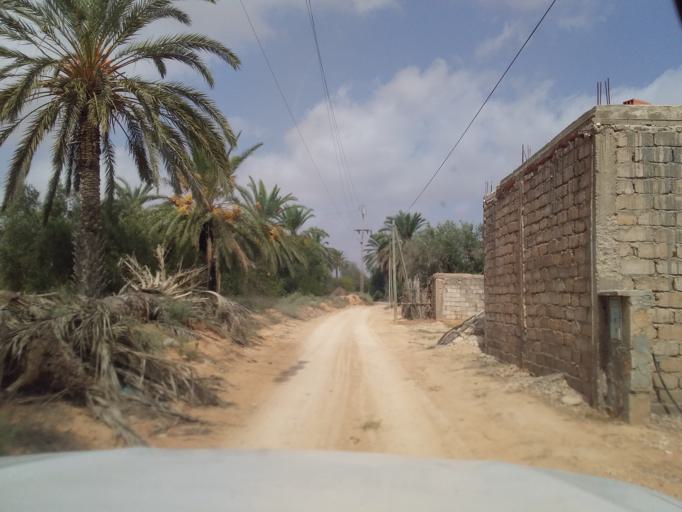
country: TN
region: Madanin
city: Medenine
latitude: 33.6250
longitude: 10.3113
